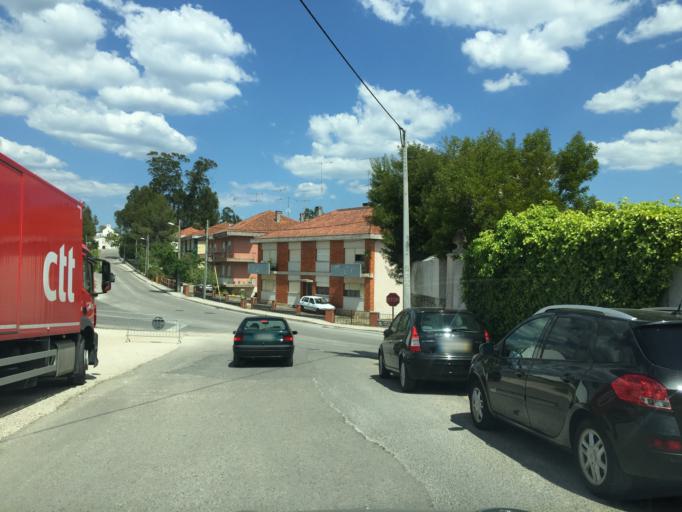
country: PT
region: Santarem
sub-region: Ourem
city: Ourem
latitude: 39.6582
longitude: -8.5738
